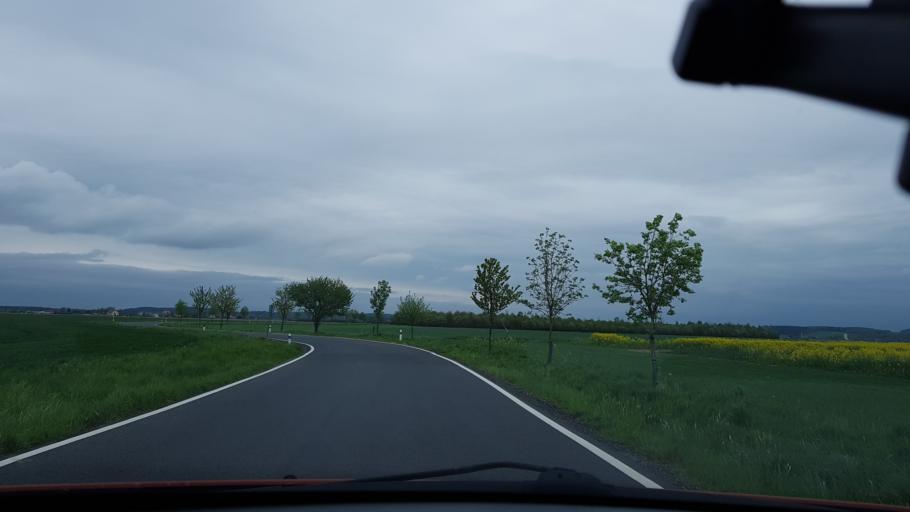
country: CZ
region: Olomoucky
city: Vidnava
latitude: 50.3807
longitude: 17.1471
